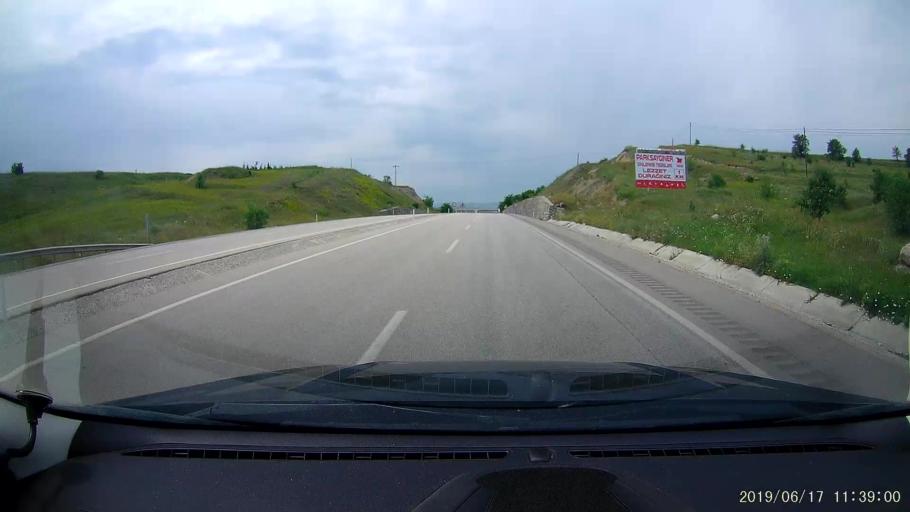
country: TR
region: Cankiri
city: Beloren
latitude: 40.8437
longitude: 33.3859
